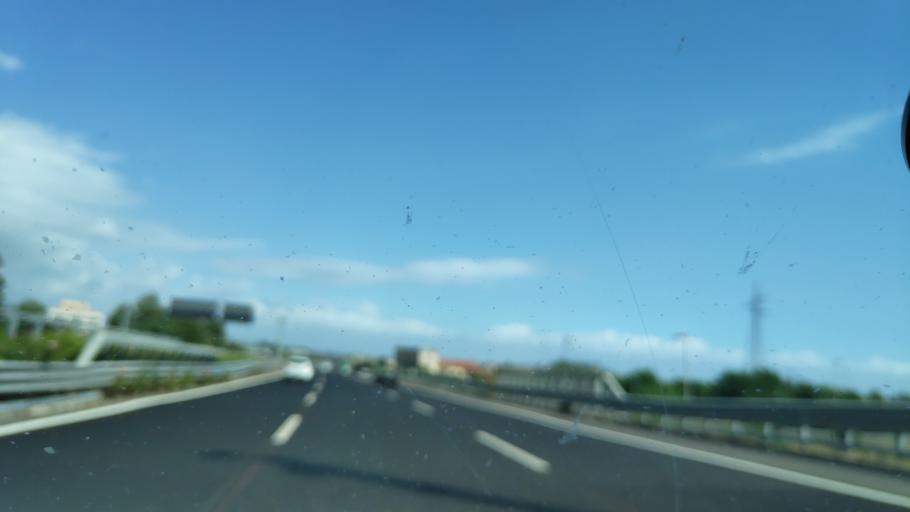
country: IT
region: Campania
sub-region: Provincia di Salerno
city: Pontecagnano
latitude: 40.6558
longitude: 14.8658
